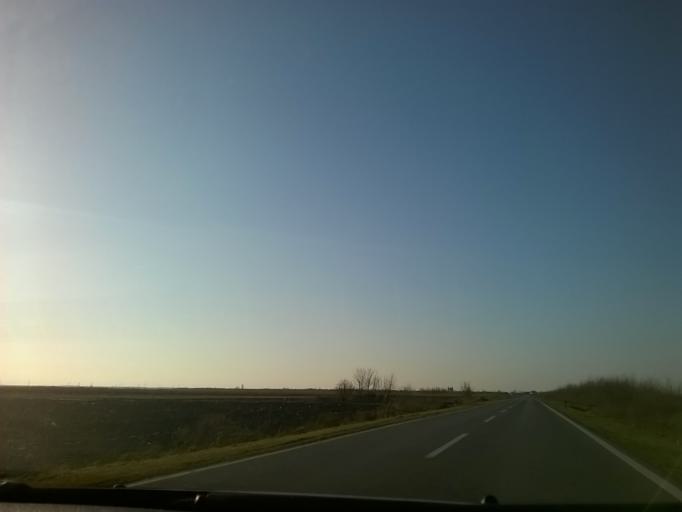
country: RS
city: Nikolinci
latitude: 45.0514
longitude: 21.0957
